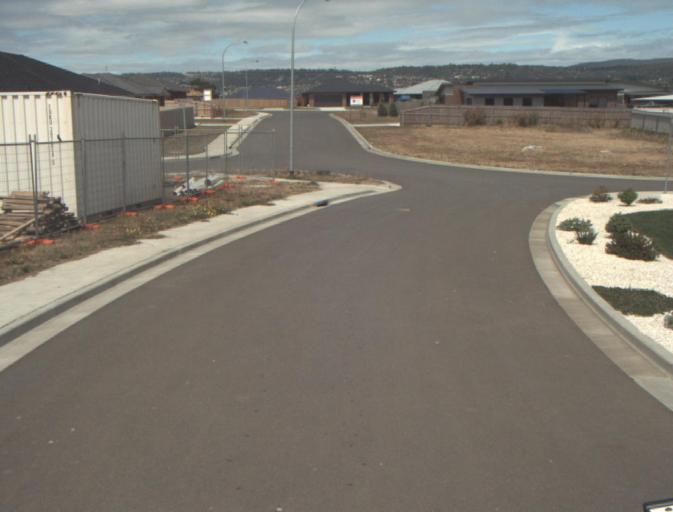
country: AU
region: Tasmania
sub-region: Launceston
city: Mayfield
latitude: -41.3808
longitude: 147.1136
